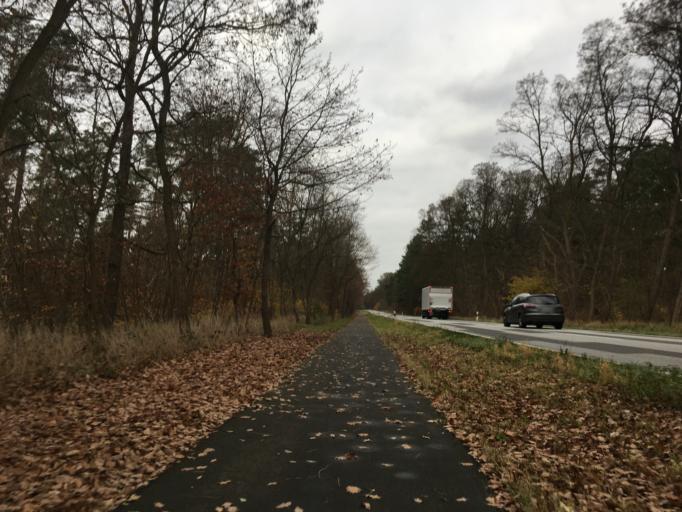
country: DE
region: Brandenburg
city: Mullrose
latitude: 52.2113
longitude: 14.4518
